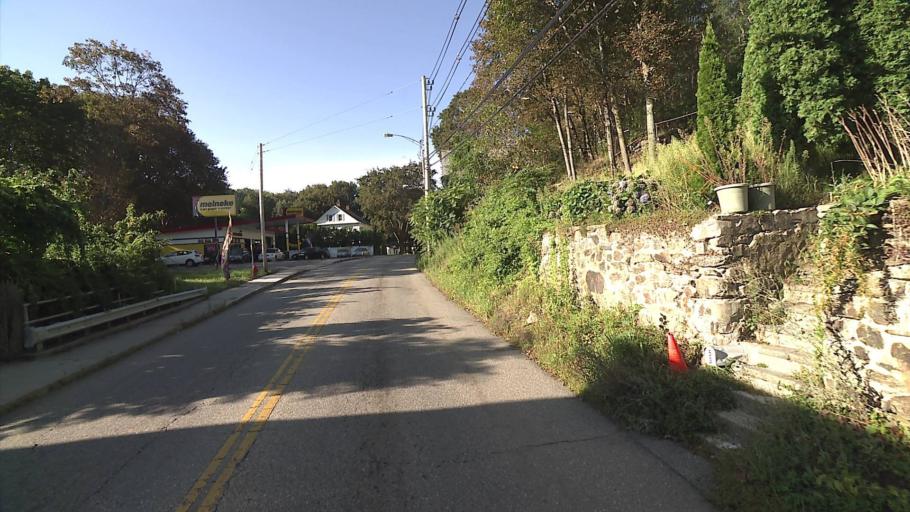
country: US
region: Connecticut
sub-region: New London County
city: Norwich
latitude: 41.5167
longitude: -72.0801
